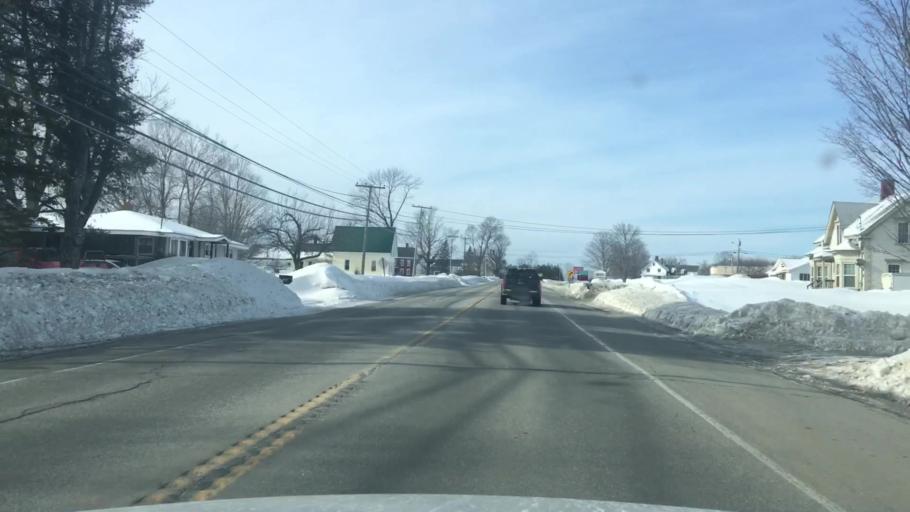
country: US
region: Maine
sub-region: Penobscot County
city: Charleston
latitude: 44.9904
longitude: -69.0157
